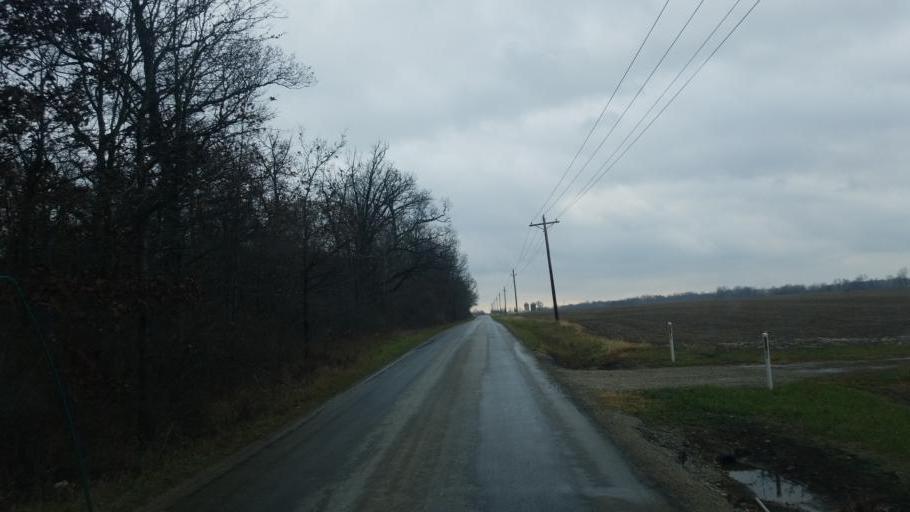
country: US
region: Indiana
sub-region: Adams County
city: Geneva
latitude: 40.5542
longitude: -84.9918
